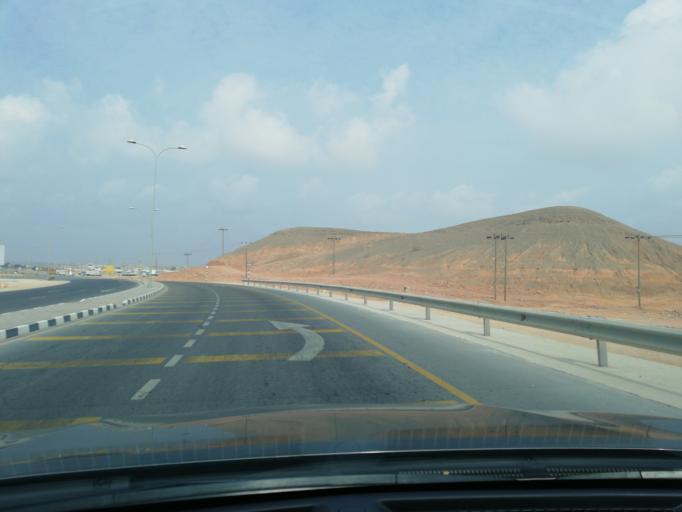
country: OM
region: Zufar
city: Salalah
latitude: 16.9507
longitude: 53.9851
